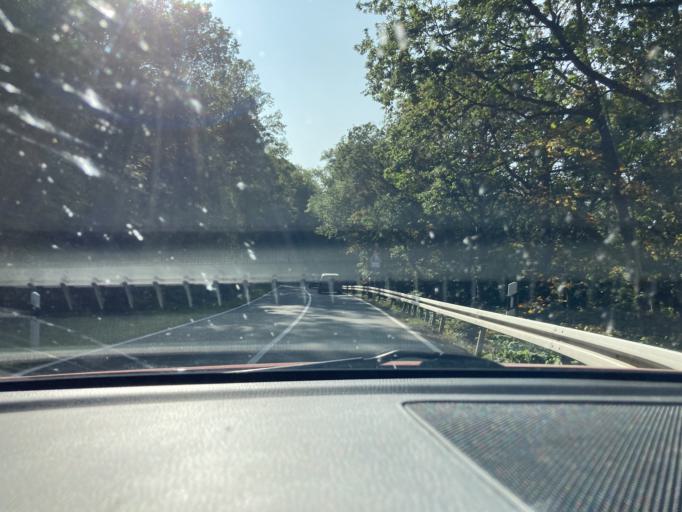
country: DE
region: Saxony-Anhalt
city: Thale
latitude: 51.7380
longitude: 11.0403
